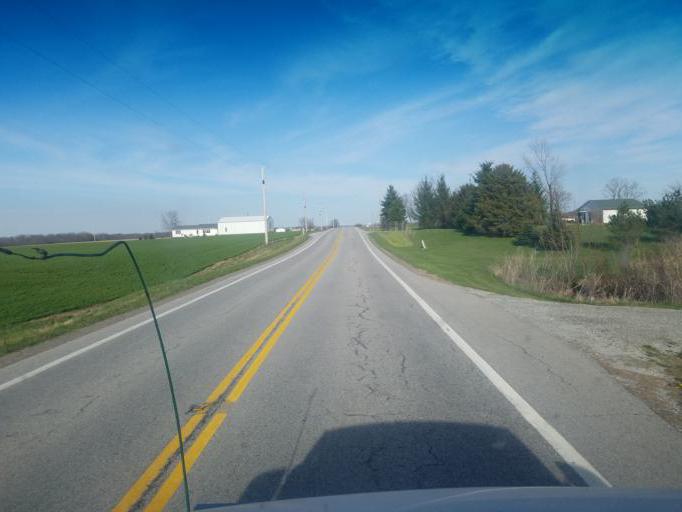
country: US
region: Ohio
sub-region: Logan County
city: De Graff
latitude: 40.3390
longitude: -83.9638
